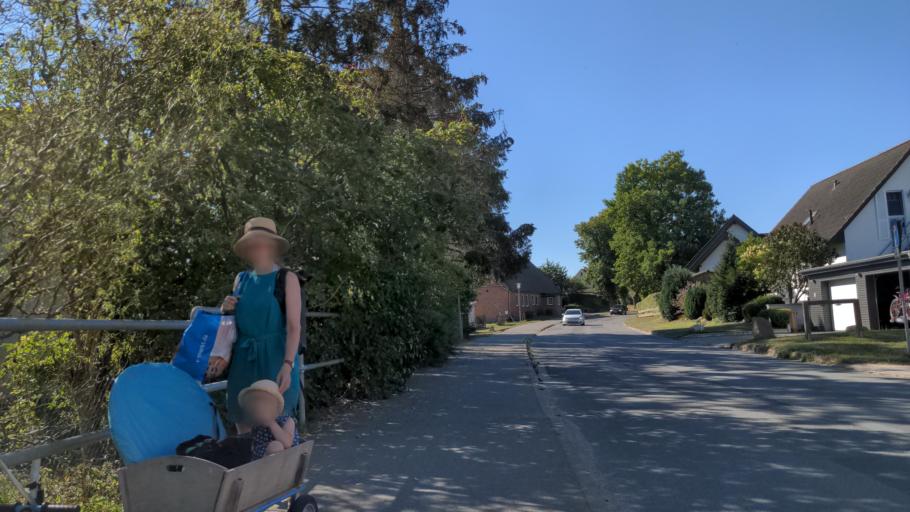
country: DE
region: Mecklenburg-Vorpommern
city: Gramkow
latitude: 53.9342
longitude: 11.3315
